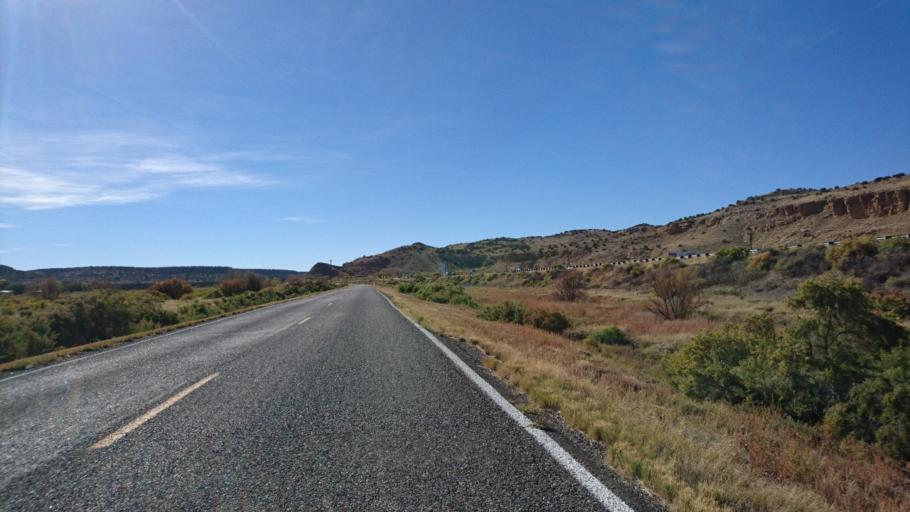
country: US
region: New Mexico
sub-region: Cibola County
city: Skyline-Ganipa
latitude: 35.0700
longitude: -107.6758
